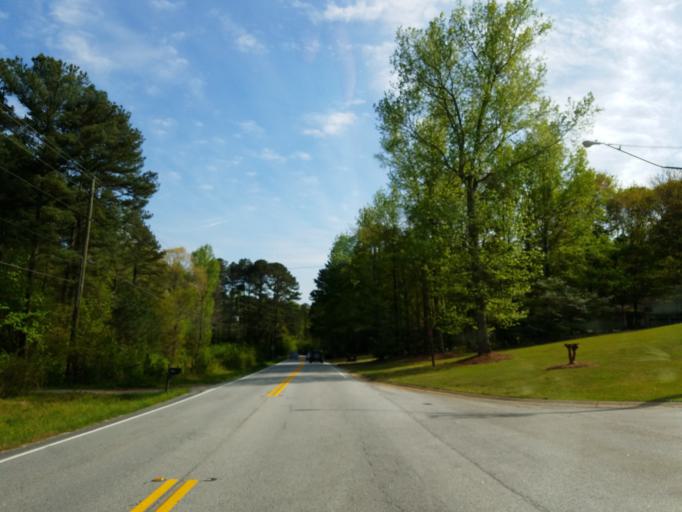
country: US
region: Georgia
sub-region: Douglas County
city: Lithia Springs
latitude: 33.7664
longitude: -84.6366
